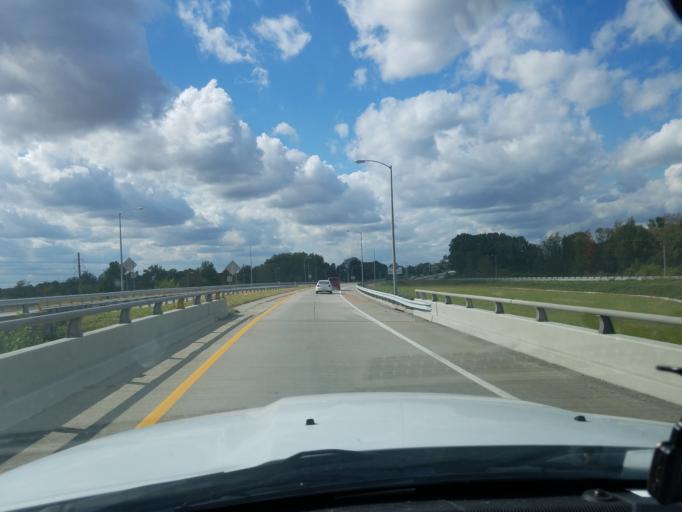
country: US
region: Kentucky
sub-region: Daviess County
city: Owensboro
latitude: 37.7657
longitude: -87.1636
